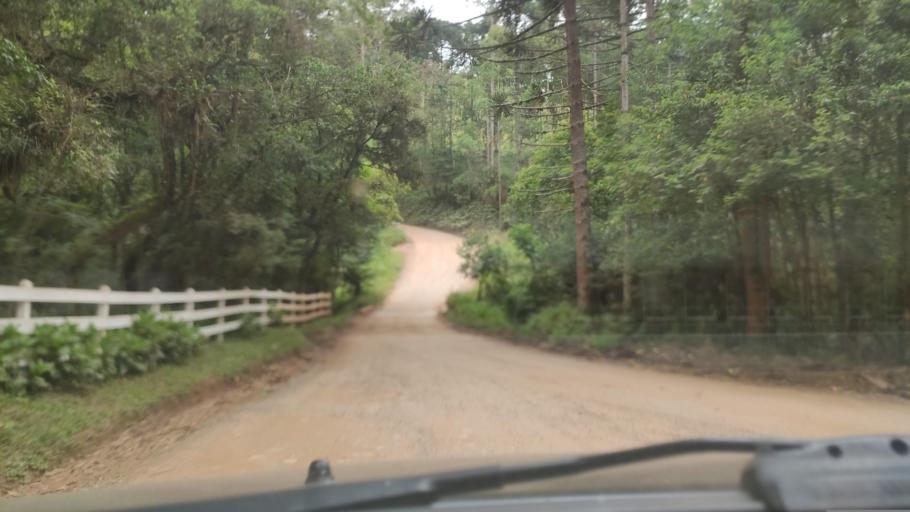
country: BR
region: Minas Gerais
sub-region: Paraisopolis
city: Paraisopolis
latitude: -22.7041
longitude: -45.8439
